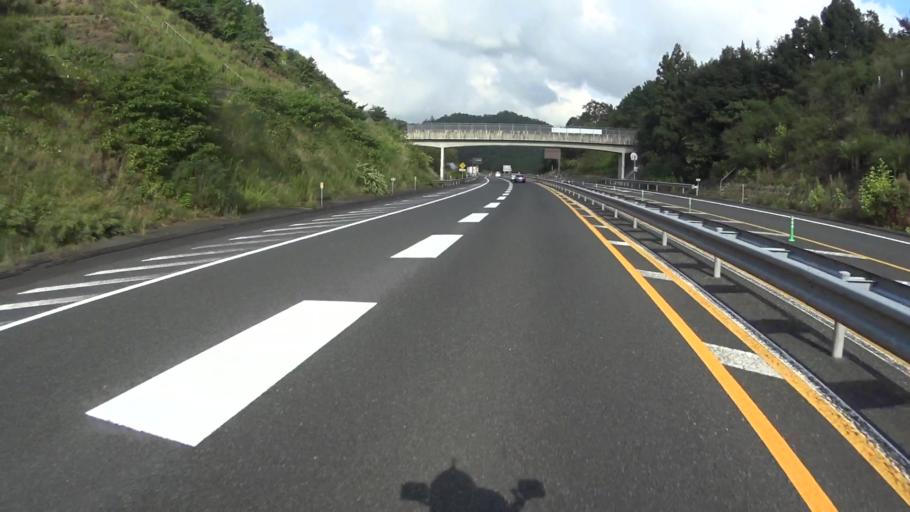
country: JP
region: Kyoto
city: Miyazu
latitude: 35.4346
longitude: 135.2034
